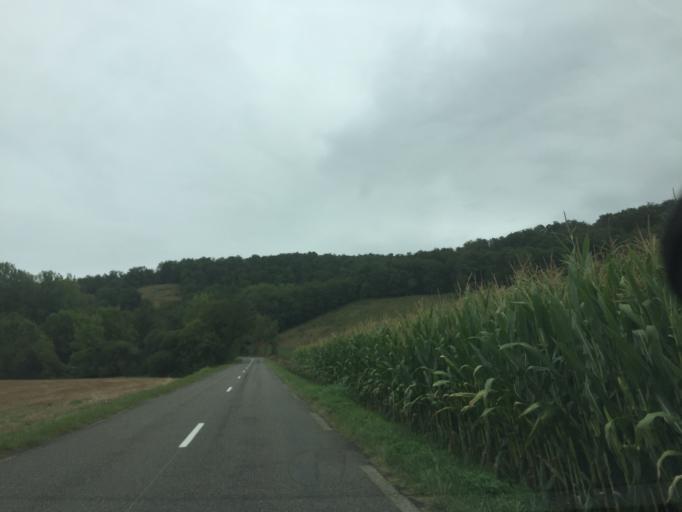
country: FR
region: Midi-Pyrenees
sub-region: Departement des Hautes-Pyrenees
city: Rabastens-de-Bigorre
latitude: 43.3544
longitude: 0.2295
